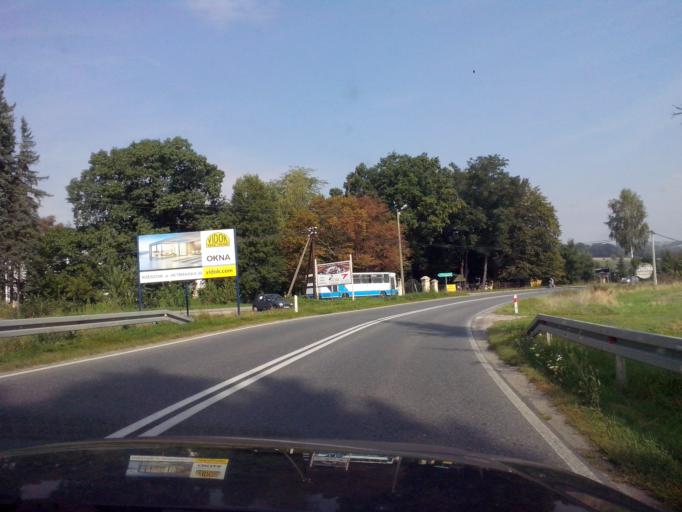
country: PL
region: Subcarpathian Voivodeship
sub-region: Powiat strzyzowski
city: Czudec
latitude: 49.9394
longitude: 21.8145
